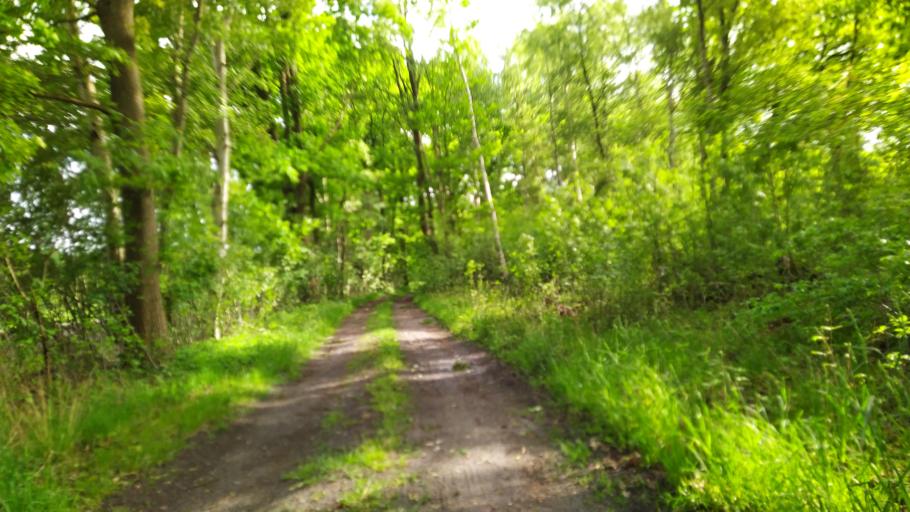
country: DE
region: Lower Saxony
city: Farven
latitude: 53.4186
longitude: 9.3476
